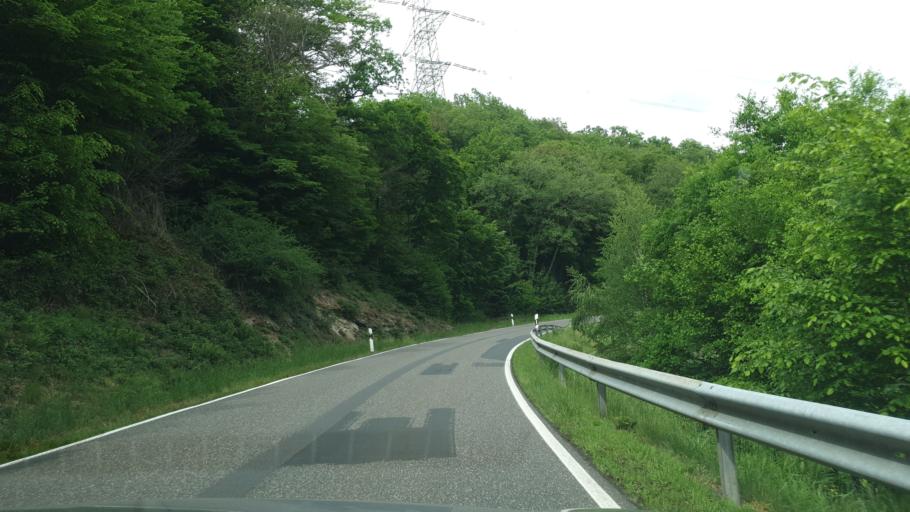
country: DE
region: Rheinland-Pfalz
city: Gackenbach
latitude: 50.3592
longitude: 7.8668
